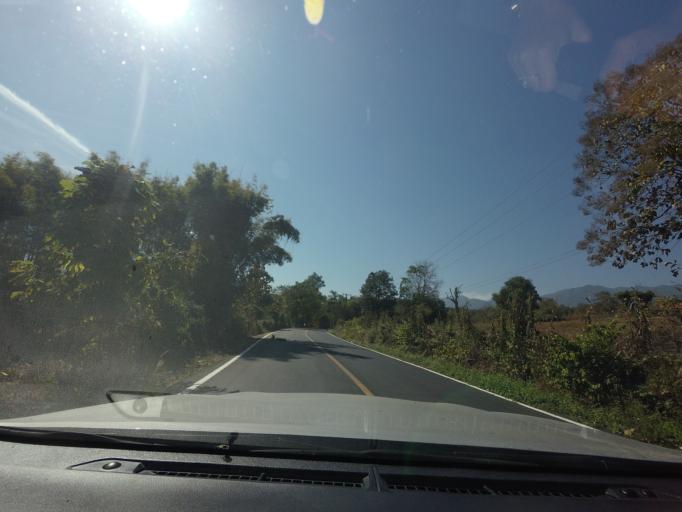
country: TH
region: Mae Hong Son
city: Wiang Nuea
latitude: 19.3798
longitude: 98.4354
